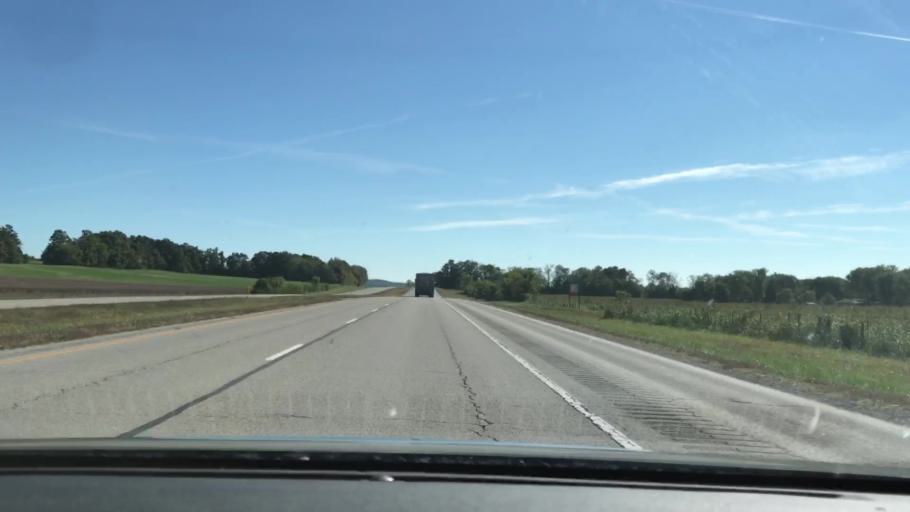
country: US
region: Kentucky
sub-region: Todd County
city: Elkton
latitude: 36.8467
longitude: -87.2981
